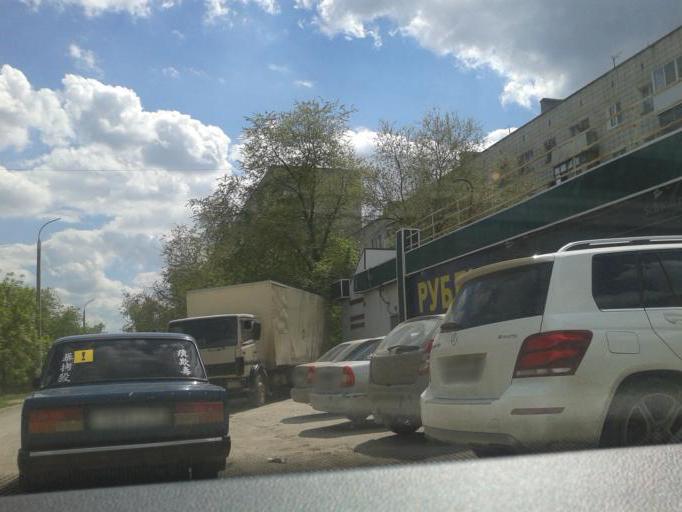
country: RU
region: Volgograd
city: Volgograd
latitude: 48.6044
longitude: 44.4213
